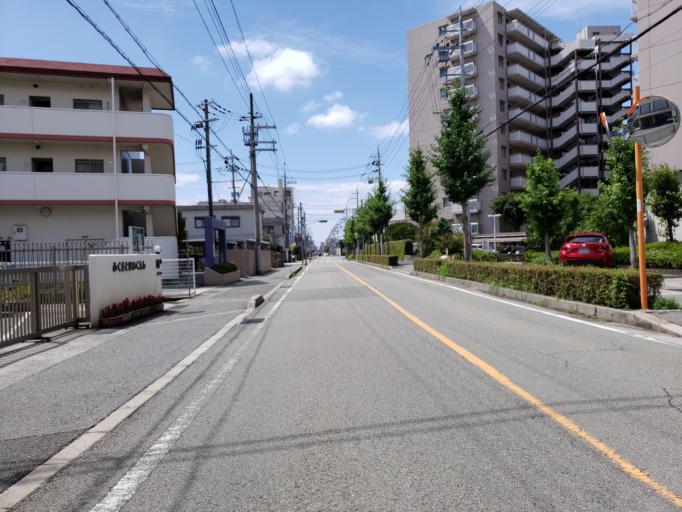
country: JP
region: Hyogo
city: Kakogawacho-honmachi
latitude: 34.7131
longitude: 134.8901
